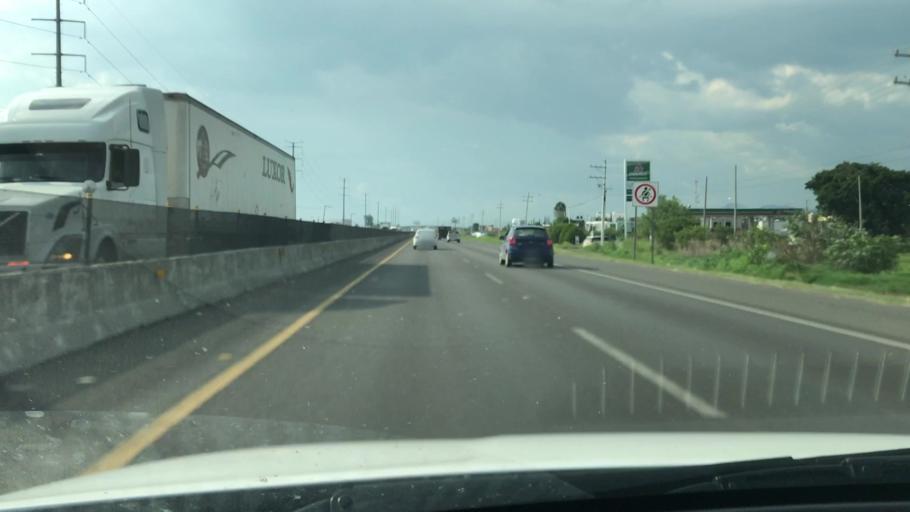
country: MX
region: Guanajuato
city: Salamanca
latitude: 20.5710
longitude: -101.2258
